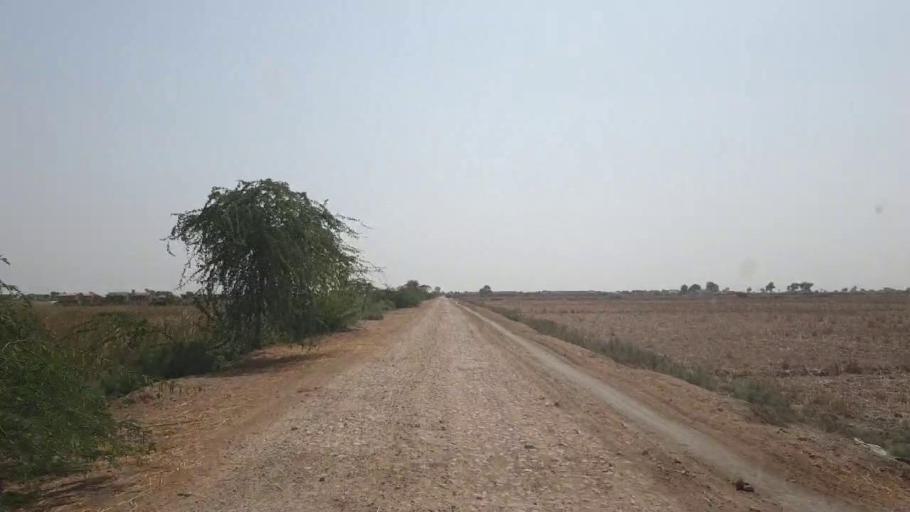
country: PK
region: Sindh
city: Jati
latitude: 24.4303
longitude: 68.5524
